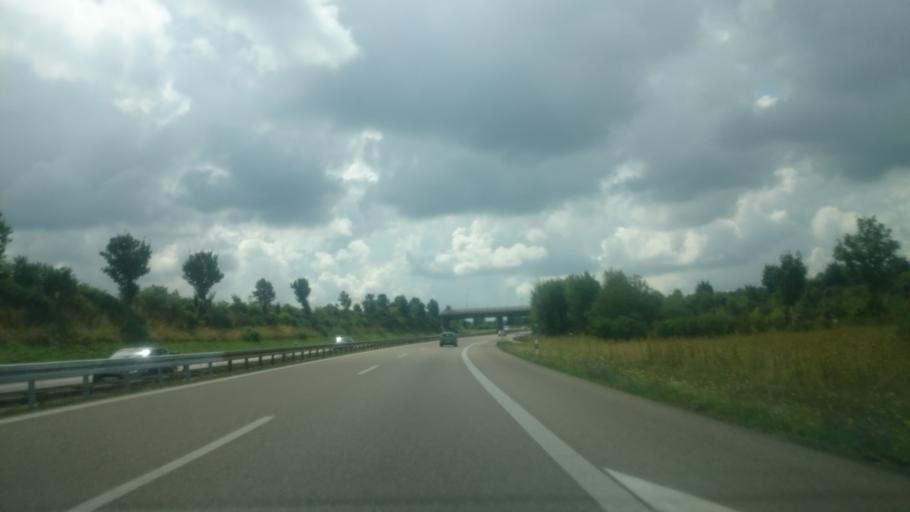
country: DE
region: Bavaria
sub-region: Swabia
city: Klosterlechfeld
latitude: 48.1591
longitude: 10.8400
